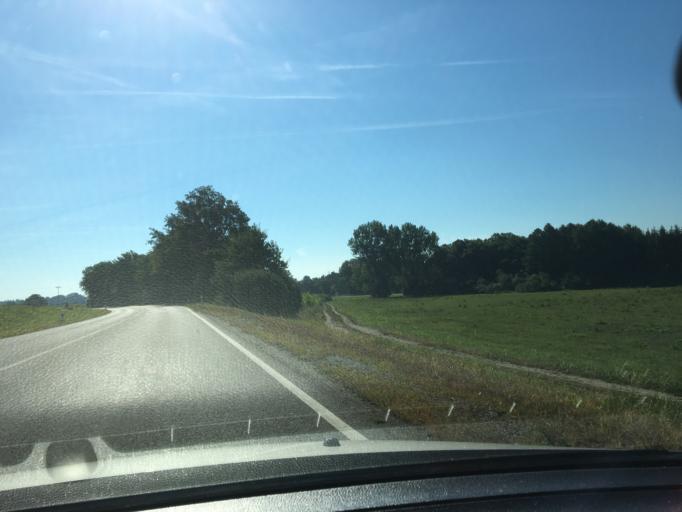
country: DE
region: Bavaria
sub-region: Upper Bavaria
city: Aham
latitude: 48.3512
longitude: 12.1893
